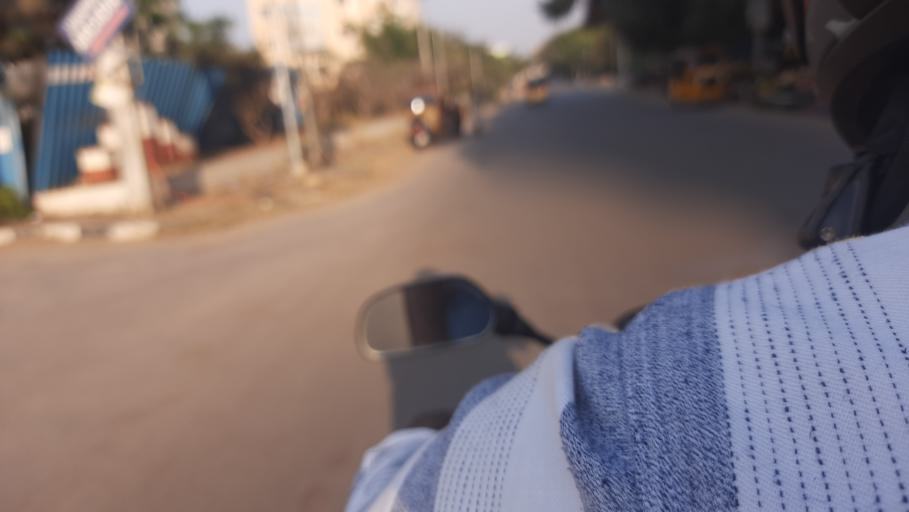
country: IN
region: Telangana
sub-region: Rangareddi
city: Secunderabad
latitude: 17.5260
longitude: 78.5376
